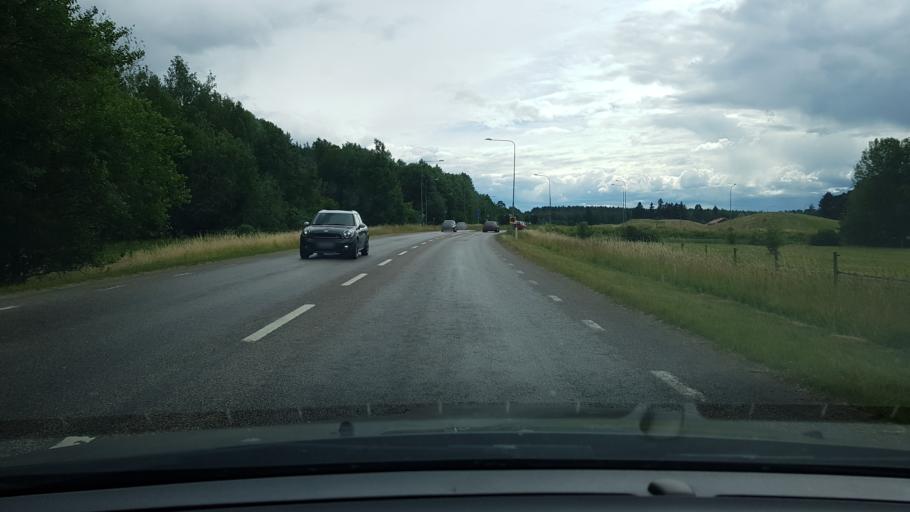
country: SE
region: Uppsala
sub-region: Uppsala Kommun
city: Saevja
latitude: 59.8184
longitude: 17.6982
